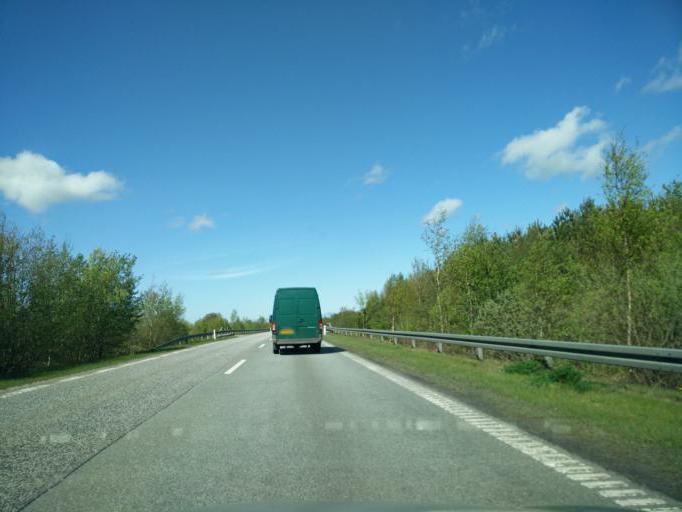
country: DK
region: Capital Region
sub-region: Gribskov Kommune
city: Helsinge
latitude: 55.9710
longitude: 12.2444
